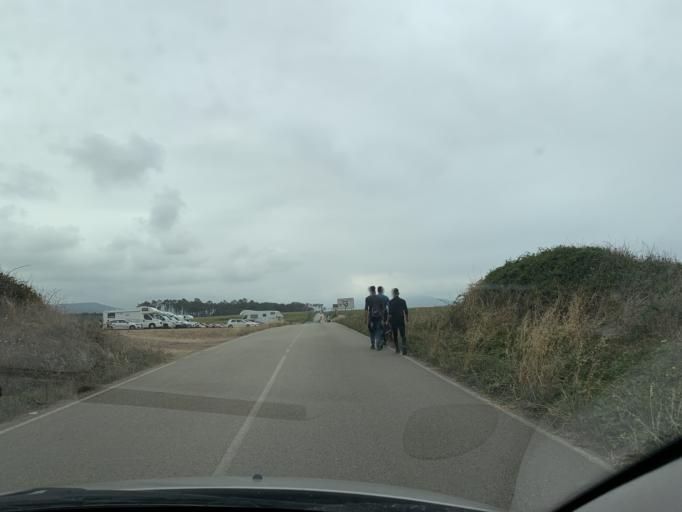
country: ES
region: Galicia
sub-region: Provincia de Lugo
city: Barreiros
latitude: 43.5525
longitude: -7.1494
